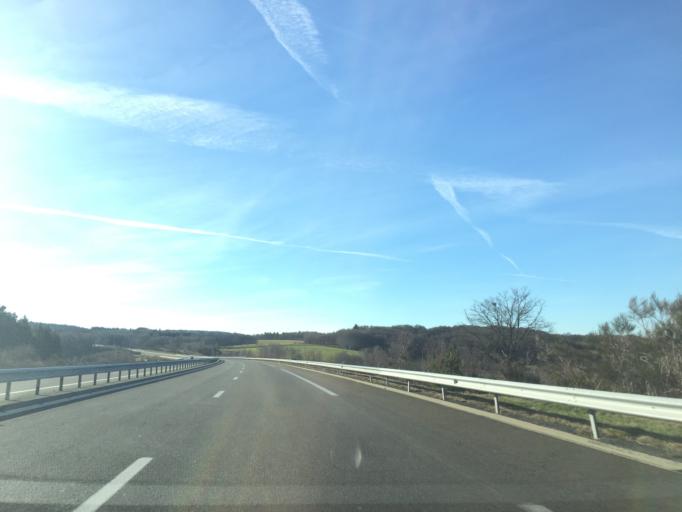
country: FR
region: Auvergne
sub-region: Departement du Puy-de-Dome
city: Gelles
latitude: 45.8185
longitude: 2.7754
